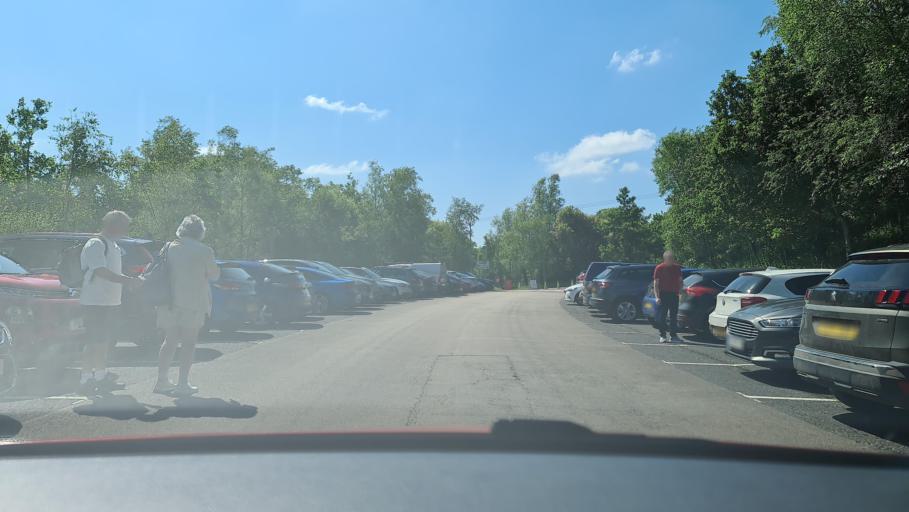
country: GB
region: England
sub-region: Cornwall
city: St Austell
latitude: 50.3585
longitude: -4.7459
